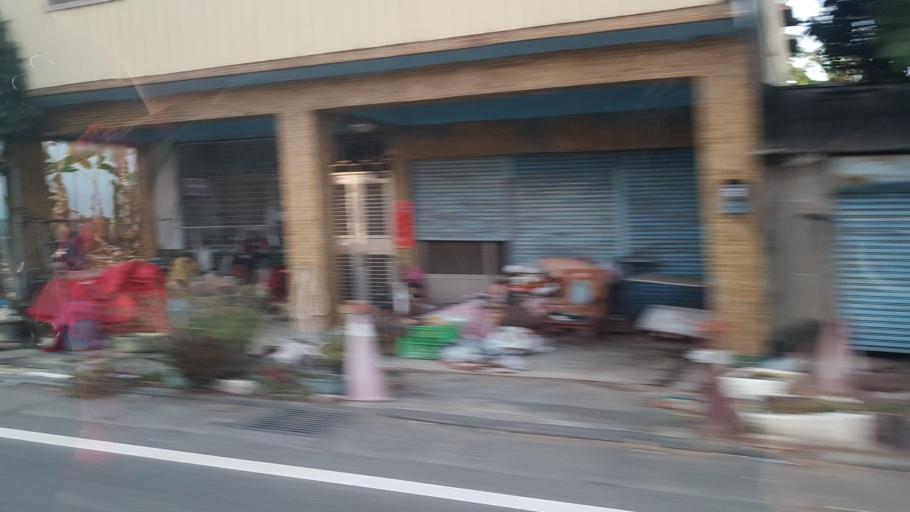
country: TW
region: Taiwan
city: Xinying
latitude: 23.3363
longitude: 120.3248
